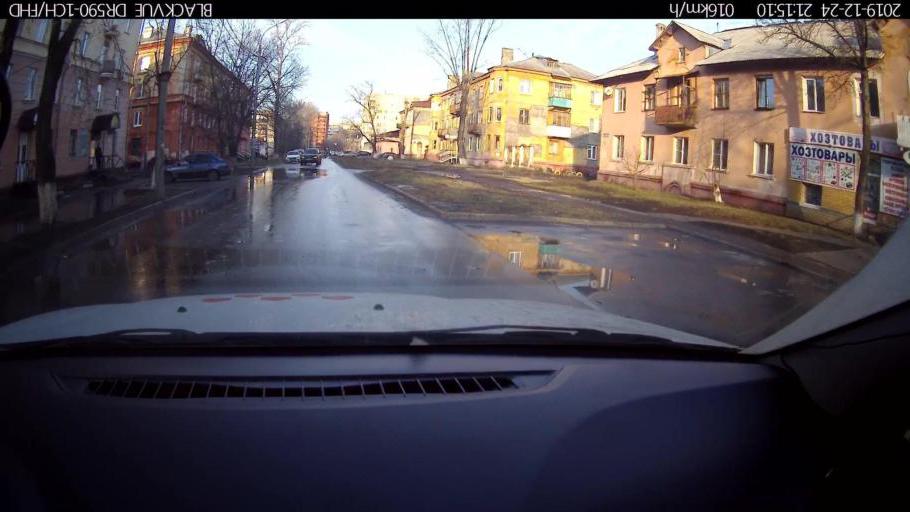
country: RU
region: Nizjnij Novgorod
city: Nizhniy Novgorod
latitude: 56.2648
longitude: 43.8870
